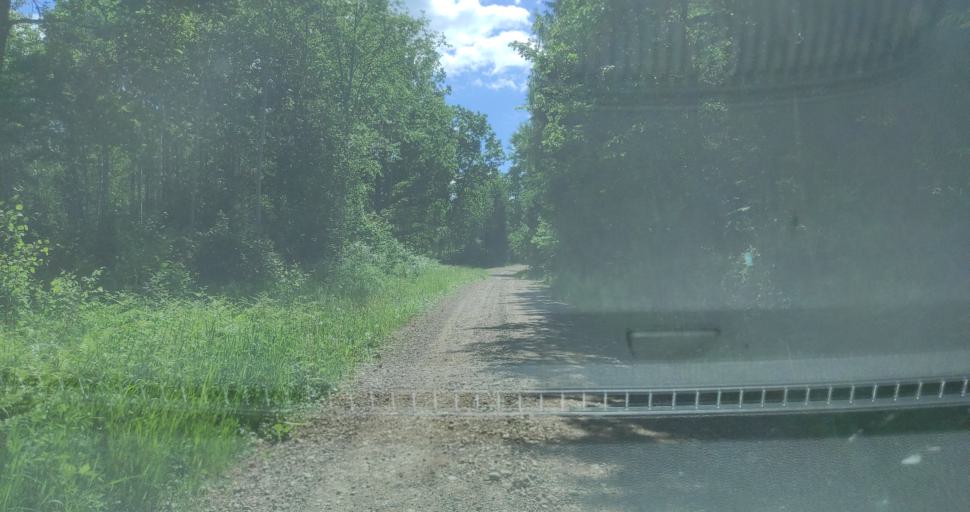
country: LV
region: Alsunga
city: Alsunga
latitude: 56.8849
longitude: 21.7244
